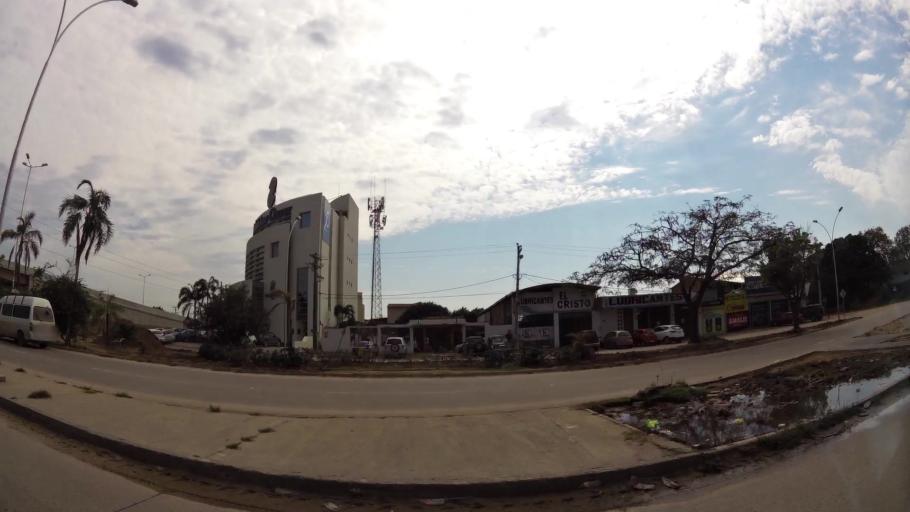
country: BO
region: Santa Cruz
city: Santa Cruz de la Sierra
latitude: -17.7408
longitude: -63.1710
